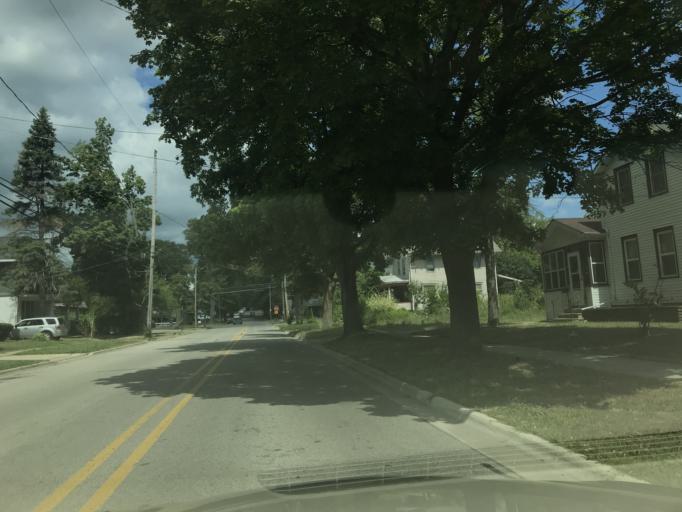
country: US
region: Michigan
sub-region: Jackson County
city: Jackson
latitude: 42.2429
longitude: -84.4185
